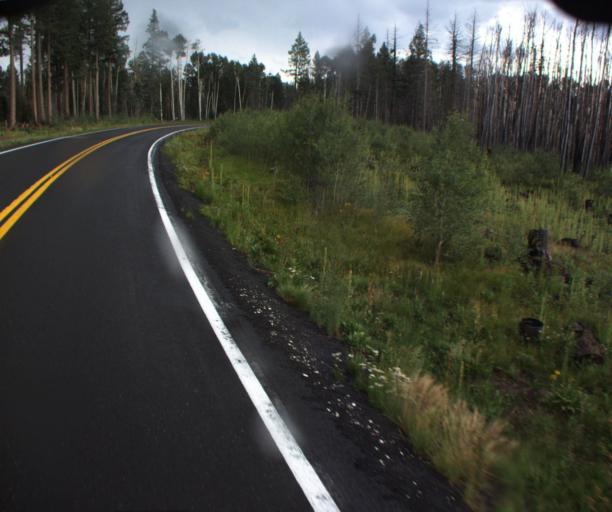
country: US
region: Arizona
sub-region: Greenlee County
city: Morenci
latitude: 33.5856
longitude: -109.3580
